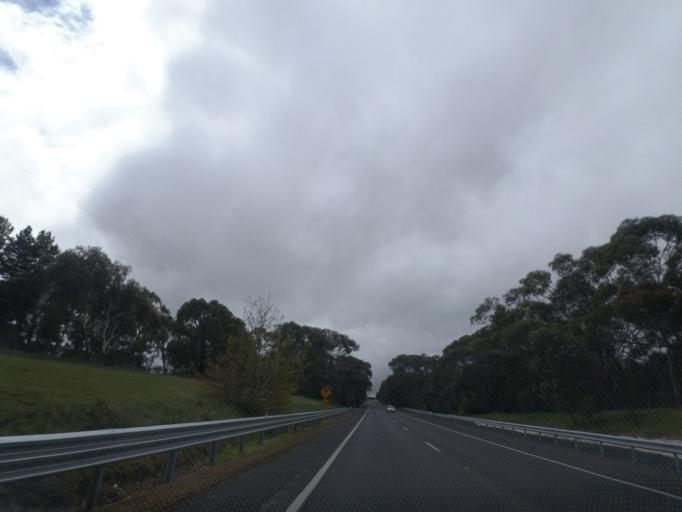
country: AU
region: Victoria
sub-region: Ballarat North
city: Soldiers Hill
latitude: -37.4590
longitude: 143.8598
